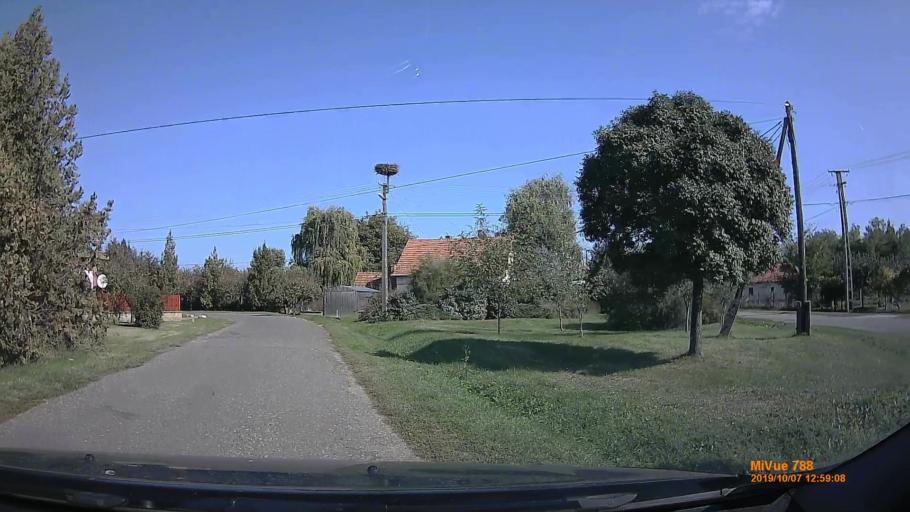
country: HU
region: Bacs-Kiskun
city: Tiszakecske
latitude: 46.8847
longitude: 20.1272
